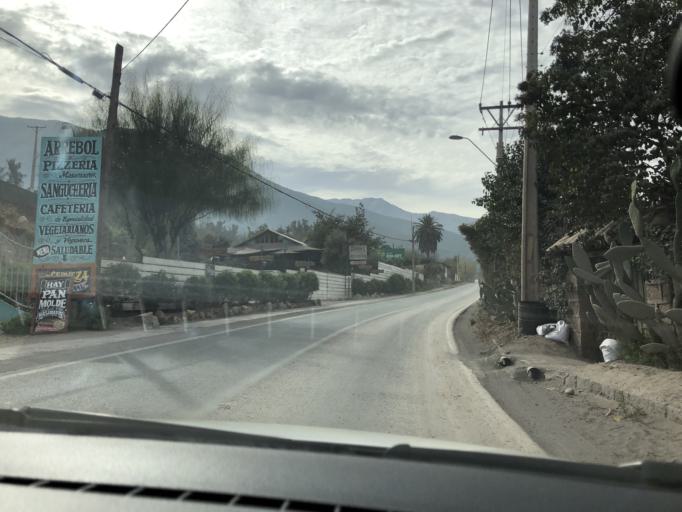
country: CL
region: Santiago Metropolitan
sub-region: Provincia de Cordillera
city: Puente Alto
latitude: -33.5946
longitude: -70.4901
